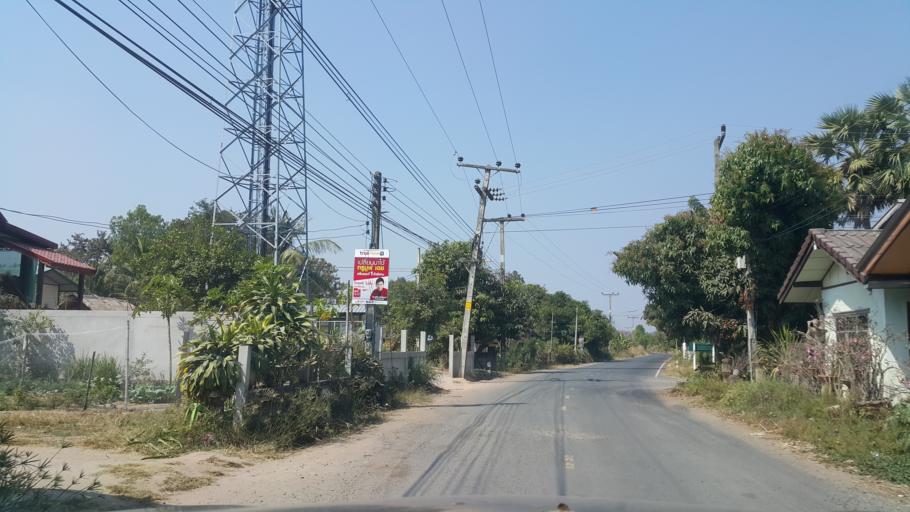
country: TH
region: Buriram
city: Satuek
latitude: 15.1314
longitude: 103.3752
